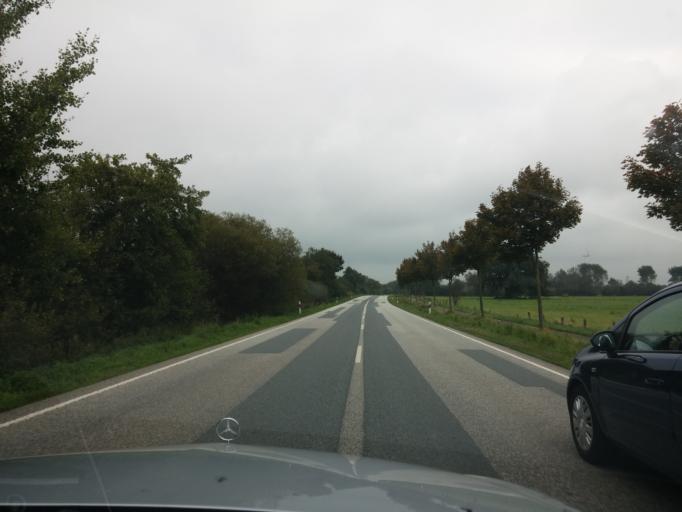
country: DE
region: Schleswig-Holstein
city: Schwesing
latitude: 54.5018
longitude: 9.1453
